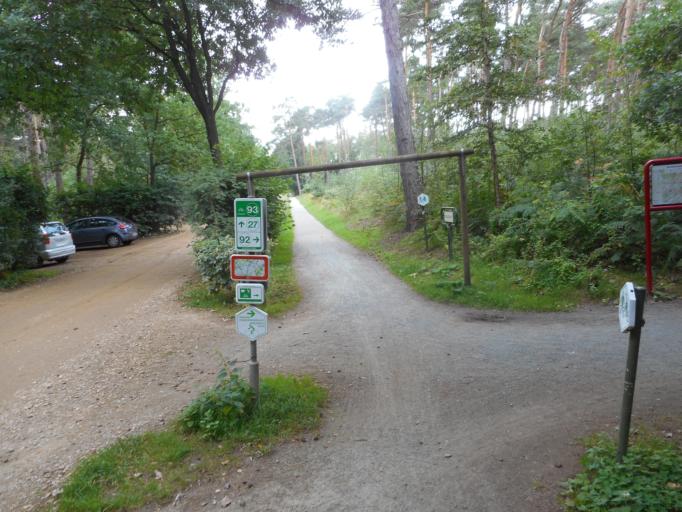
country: BE
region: Flanders
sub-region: Provincie Antwerpen
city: Zandhoven
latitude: 51.2432
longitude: 4.6762
